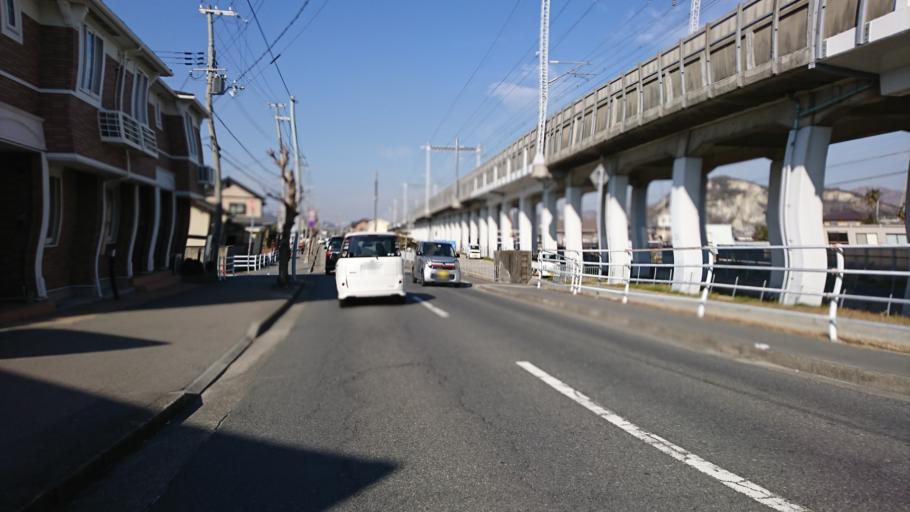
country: JP
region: Hyogo
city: Kakogawacho-honmachi
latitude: 34.7715
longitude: 134.7931
